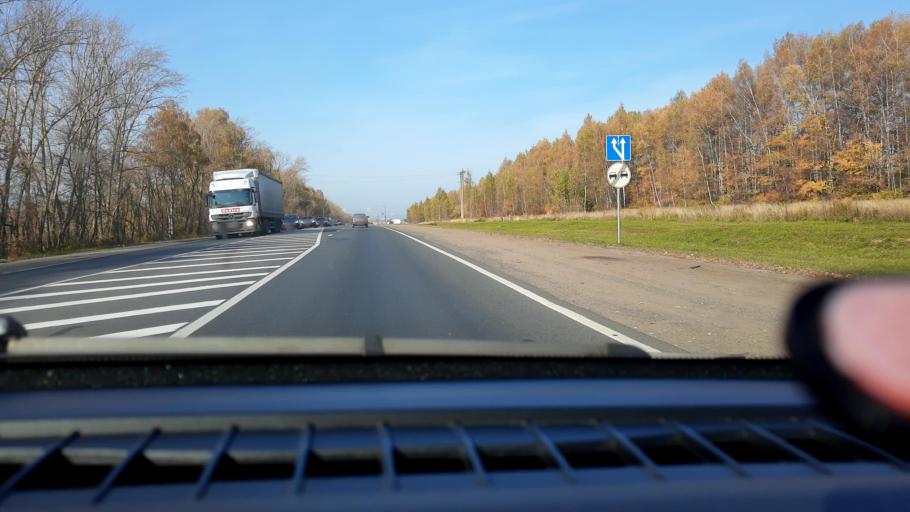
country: RU
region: Nizjnij Novgorod
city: Kstovo
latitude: 56.1127
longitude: 44.2815
